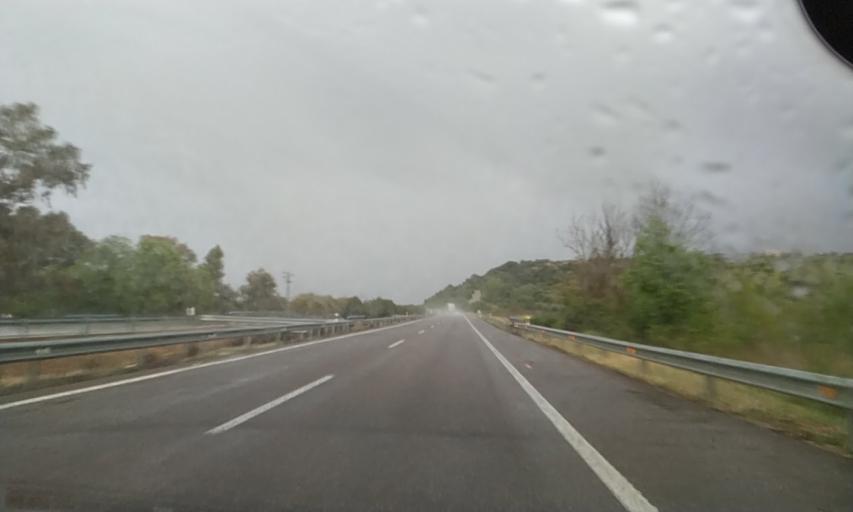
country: ES
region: Extremadura
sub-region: Provincia de Badajoz
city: Lobon
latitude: 38.8583
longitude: -6.5804
